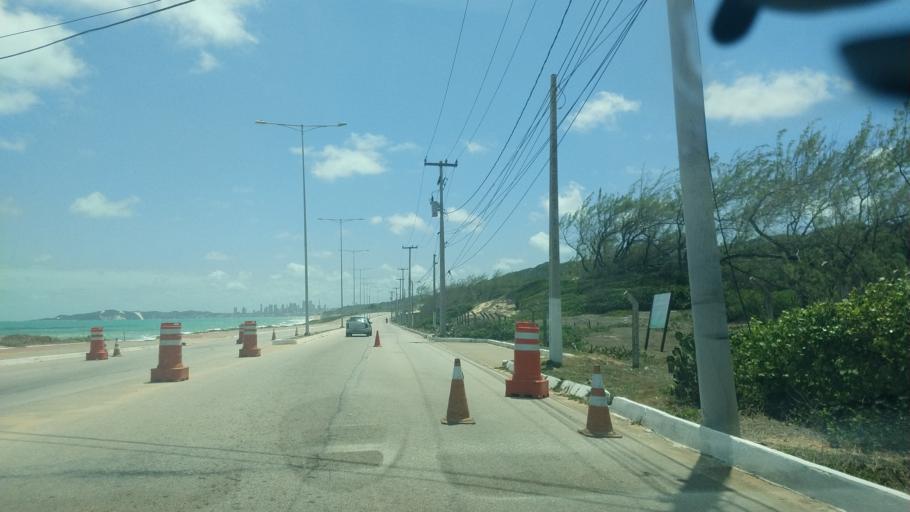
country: BR
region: Rio Grande do Norte
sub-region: Natal
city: Natal
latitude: -5.8113
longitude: -35.1820
